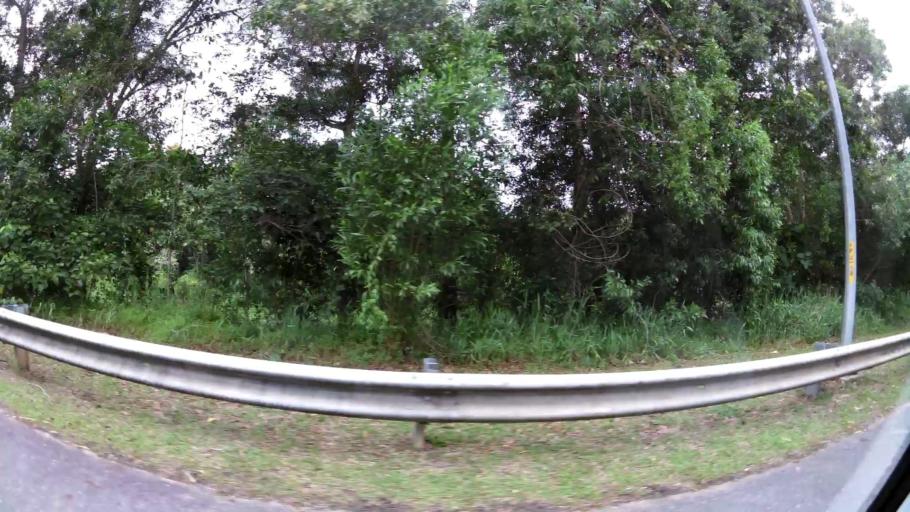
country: BN
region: Brunei and Muara
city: Bandar Seri Begawan
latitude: 4.8853
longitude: 114.9115
